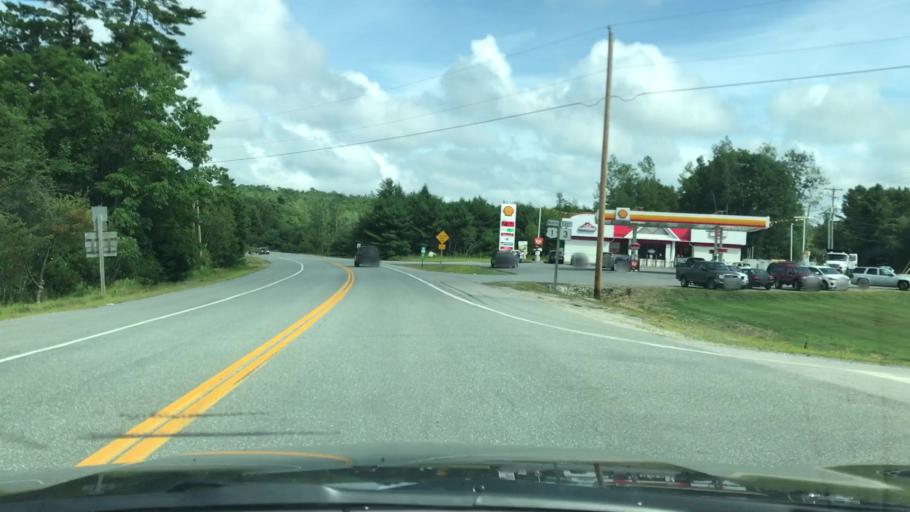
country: US
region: Maine
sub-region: Hancock County
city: Orland
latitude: 44.5601
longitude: -68.7091
